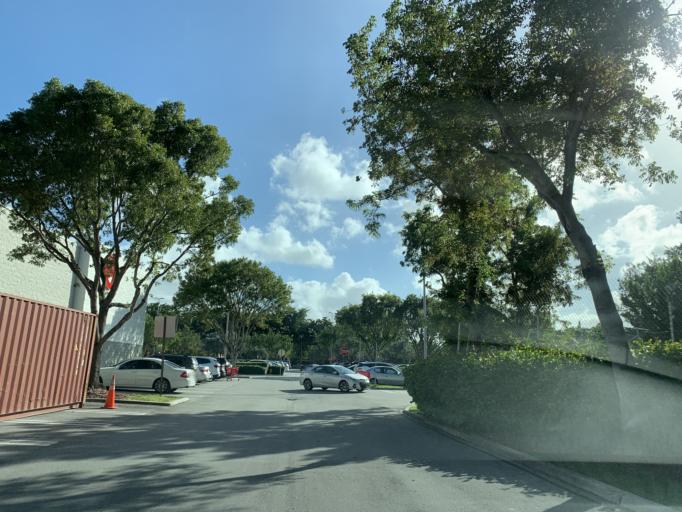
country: US
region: Florida
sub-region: Miami-Dade County
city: The Hammocks
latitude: 25.6860
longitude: -80.4383
